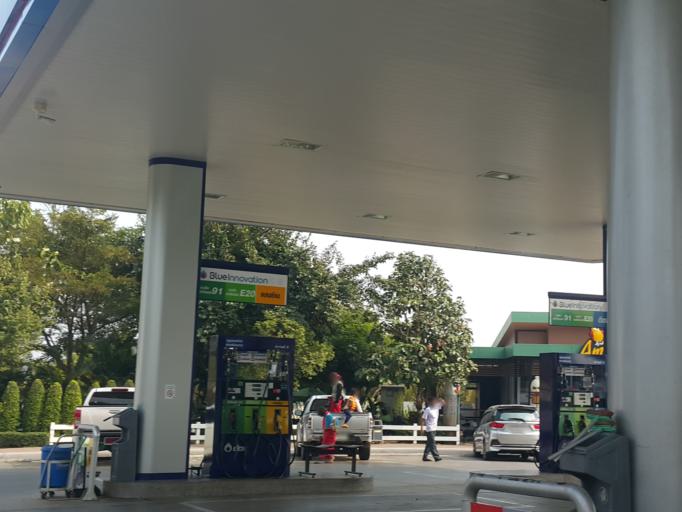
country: TH
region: Chiang Mai
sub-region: Amphoe Chiang Dao
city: Chiang Dao
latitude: 19.3534
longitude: 98.9637
